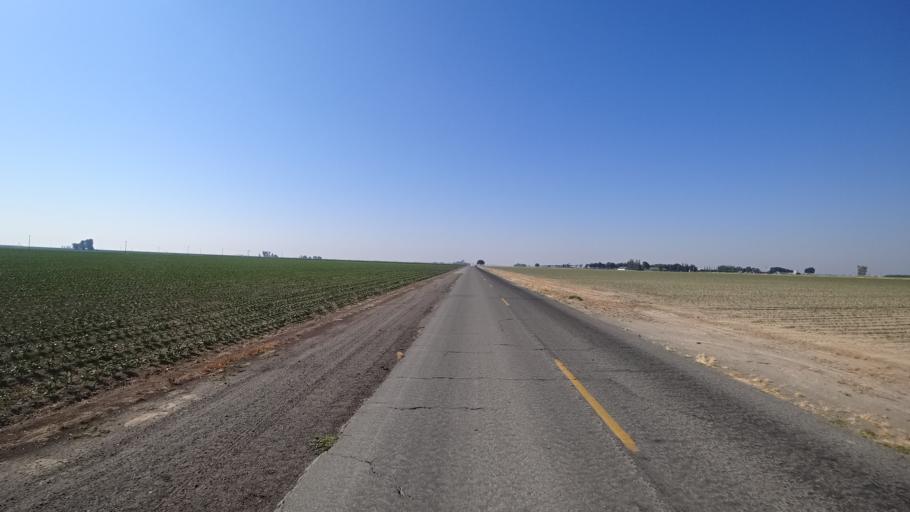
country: US
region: California
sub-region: Fresno County
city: Kingsburg
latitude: 36.4214
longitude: -119.5285
